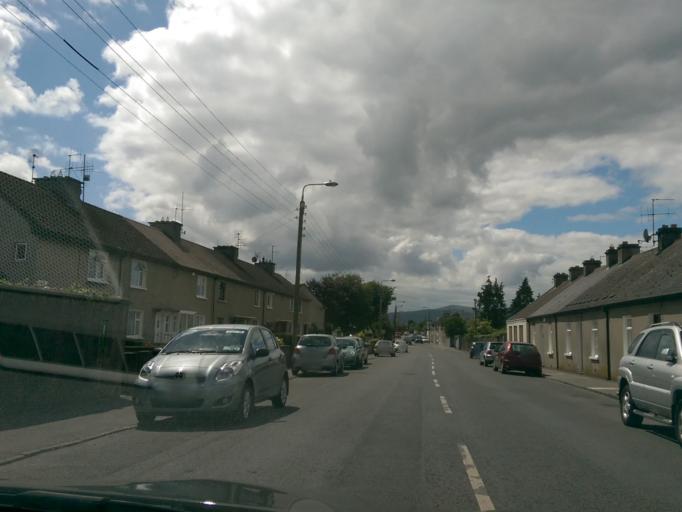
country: IE
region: Munster
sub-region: North Tipperary
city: Nenagh
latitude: 52.8603
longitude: -8.2031
